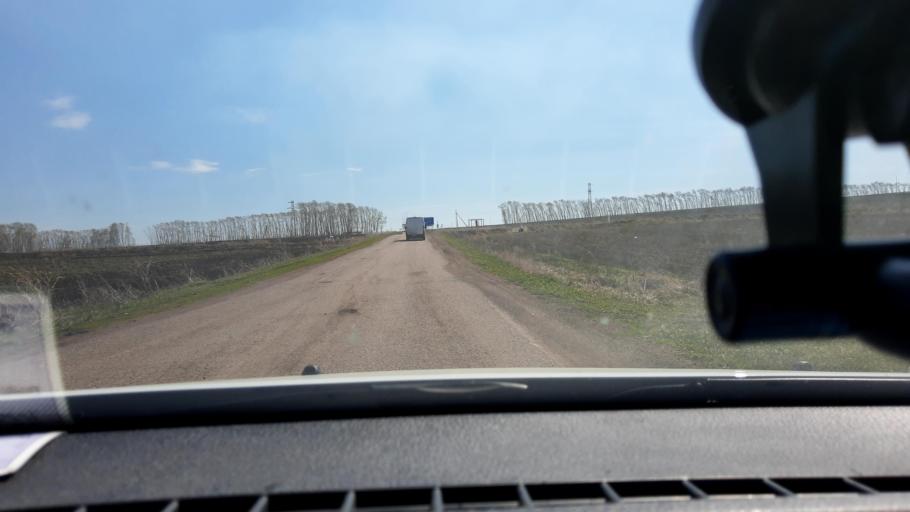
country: RU
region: Bashkortostan
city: Alekseyevka
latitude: 54.7295
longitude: 54.9215
